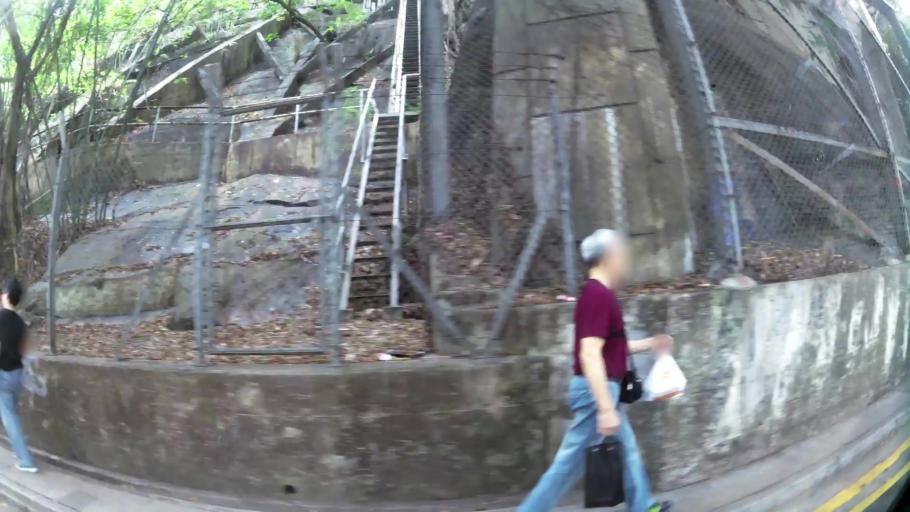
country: HK
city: Hong Kong
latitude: 22.2843
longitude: 114.1313
